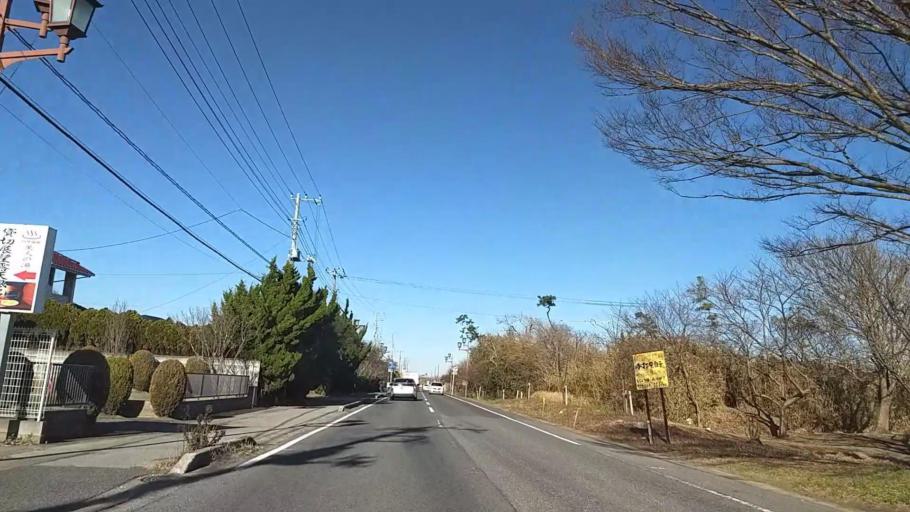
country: JP
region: Chiba
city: Mobara
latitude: 35.4323
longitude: 140.3966
